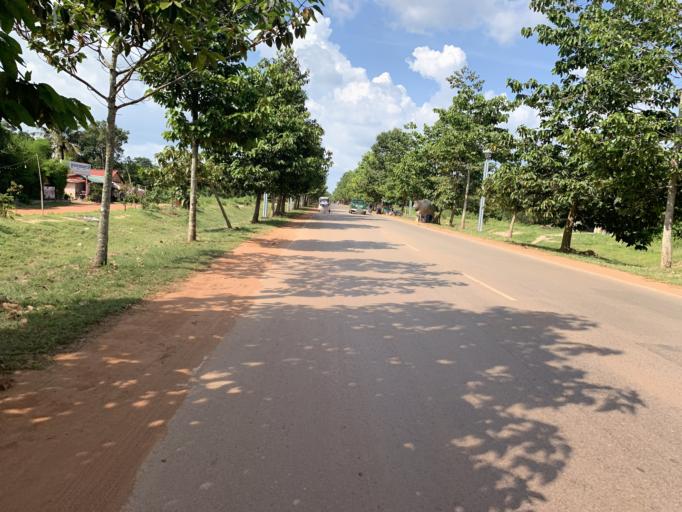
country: KH
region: Siem Reap
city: Siem Reap
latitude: 13.3837
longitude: 103.8793
